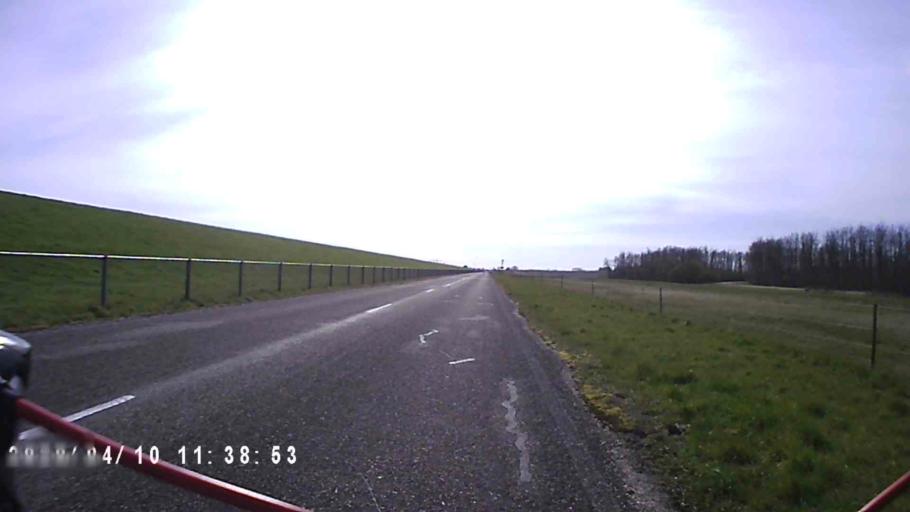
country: NL
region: Groningen
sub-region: Gemeente De Marne
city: Ulrum
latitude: 53.3970
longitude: 6.3009
